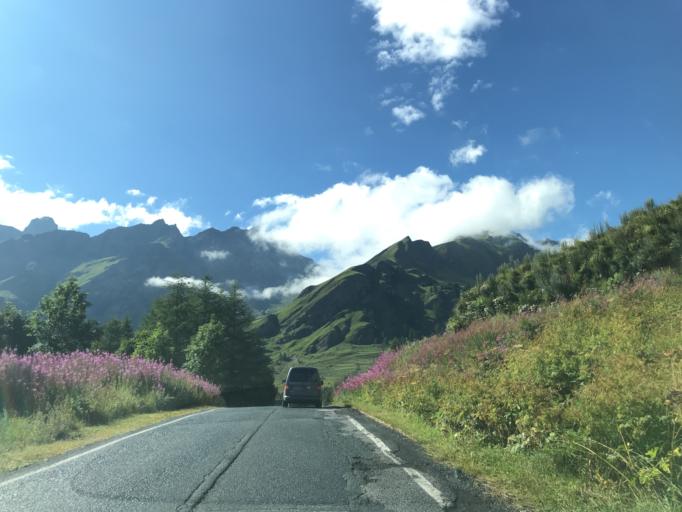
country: IT
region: Piedmont
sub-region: Provincia di Cuneo
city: Pontechianale
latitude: 44.6483
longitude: 6.9976
